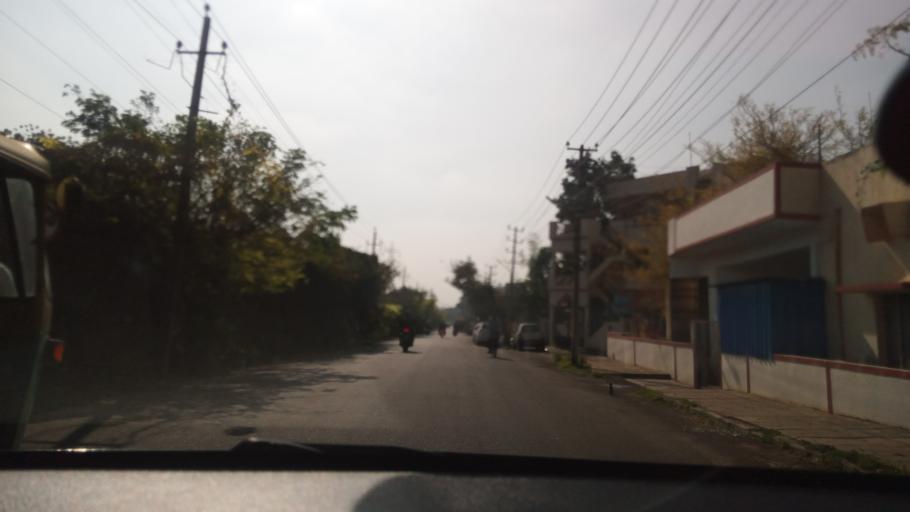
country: IN
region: Karnataka
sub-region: Bangalore Urban
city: Yelahanka
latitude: 13.0475
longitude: 77.5503
